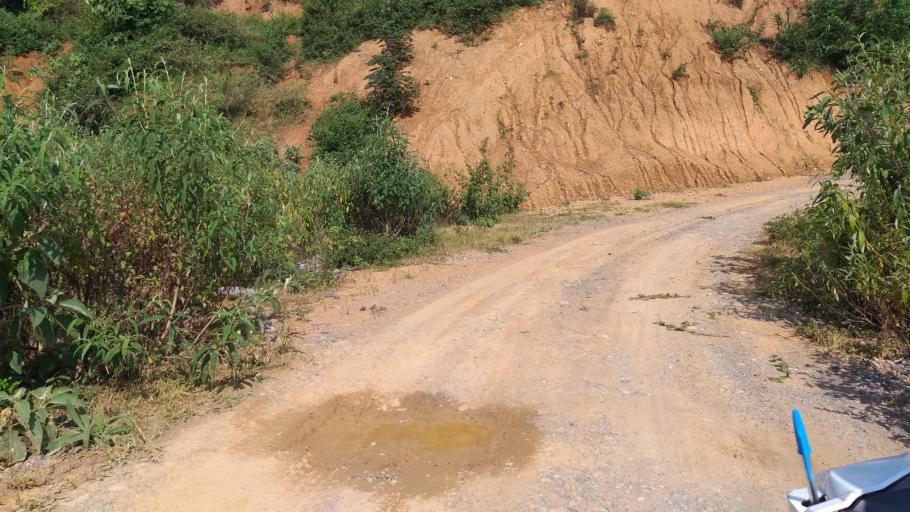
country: LA
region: Phongsali
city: Khoa
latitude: 21.2202
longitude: 102.5990
